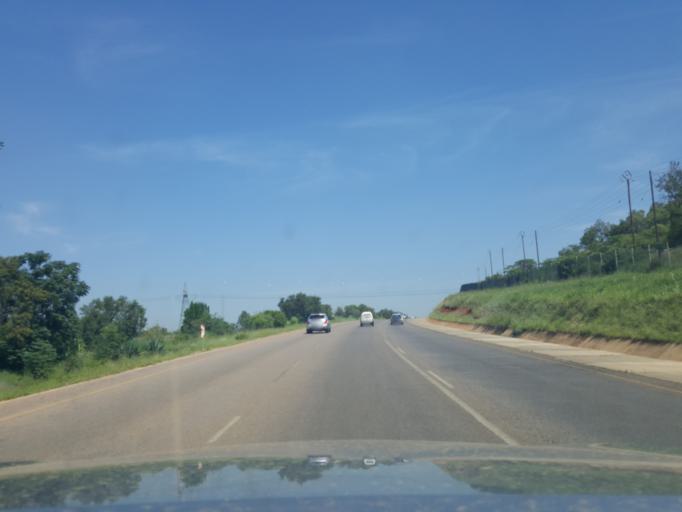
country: ZA
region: Gauteng
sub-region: City of Tshwane Metropolitan Municipality
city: Pretoria
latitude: -25.6774
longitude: 28.3483
